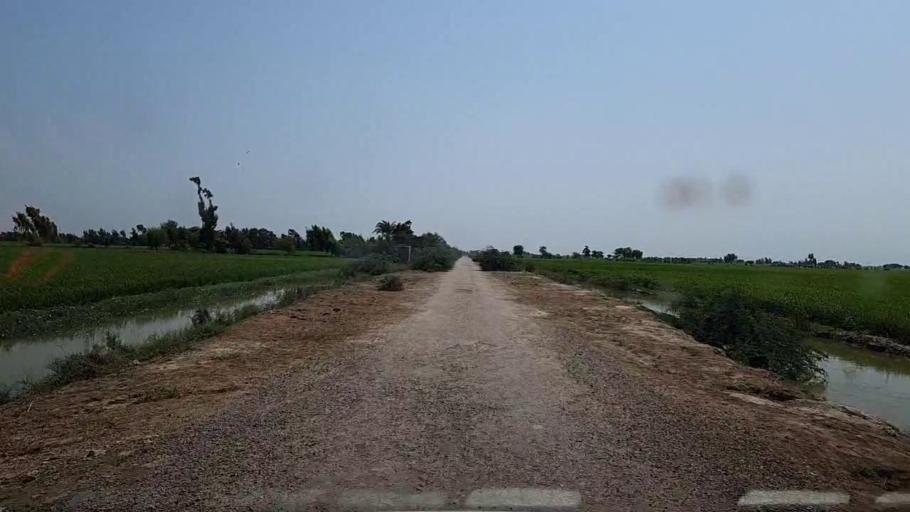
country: PK
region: Sindh
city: Mirpur Batoro
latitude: 24.6140
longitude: 68.4523
